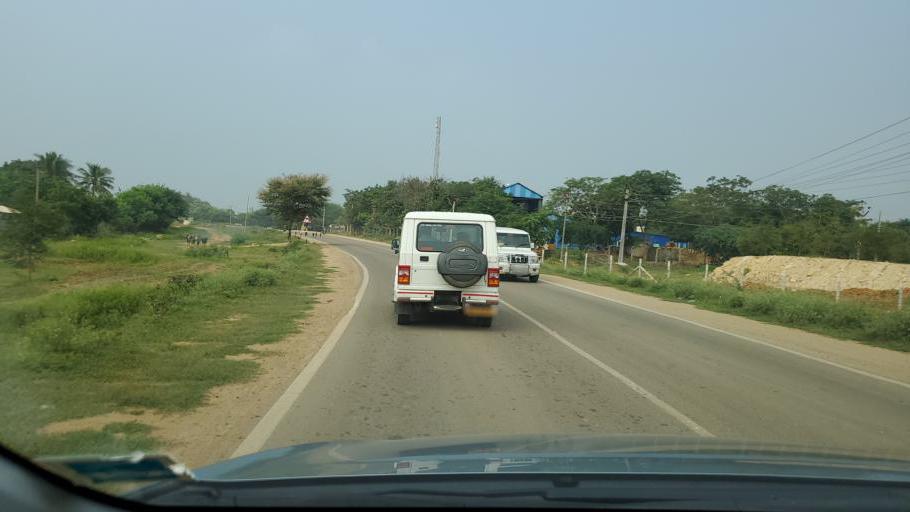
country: IN
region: Tamil Nadu
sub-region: Ariyalur
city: Ariyalur
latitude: 11.1236
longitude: 79.1416
